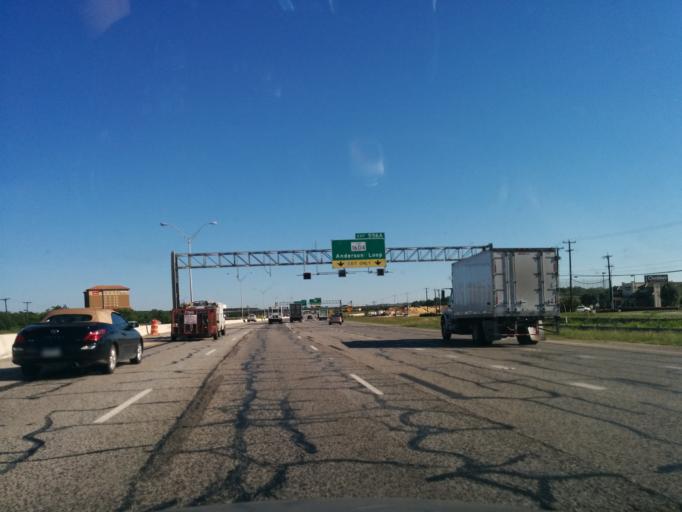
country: US
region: Texas
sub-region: Bexar County
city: Shavano Park
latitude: 29.5832
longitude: -98.5972
